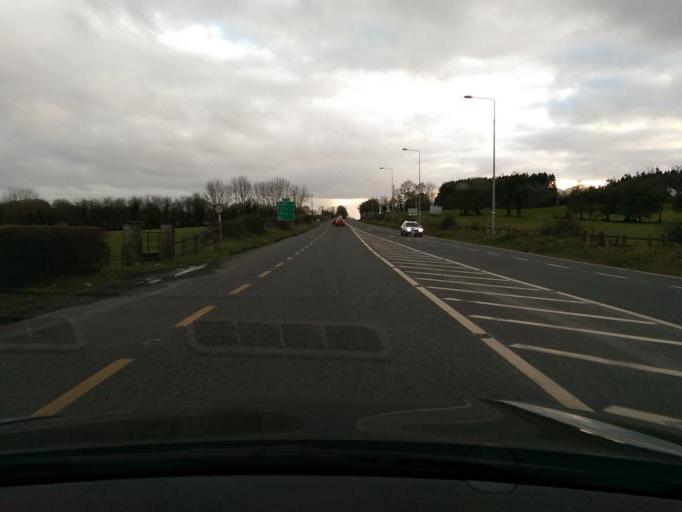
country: IE
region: Leinster
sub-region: Uibh Fhaili
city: Birr
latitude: 53.1174
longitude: -7.8901
